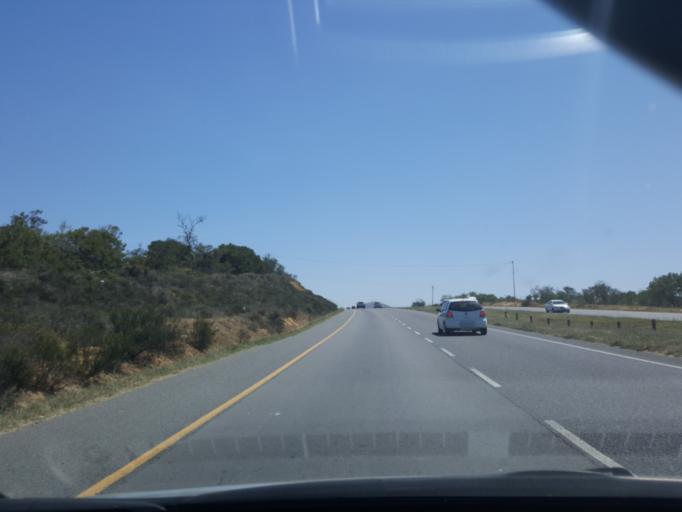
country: ZA
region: Western Cape
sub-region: City of Cape Town
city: Sunset Beach
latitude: -33.7878
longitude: 18.5488
